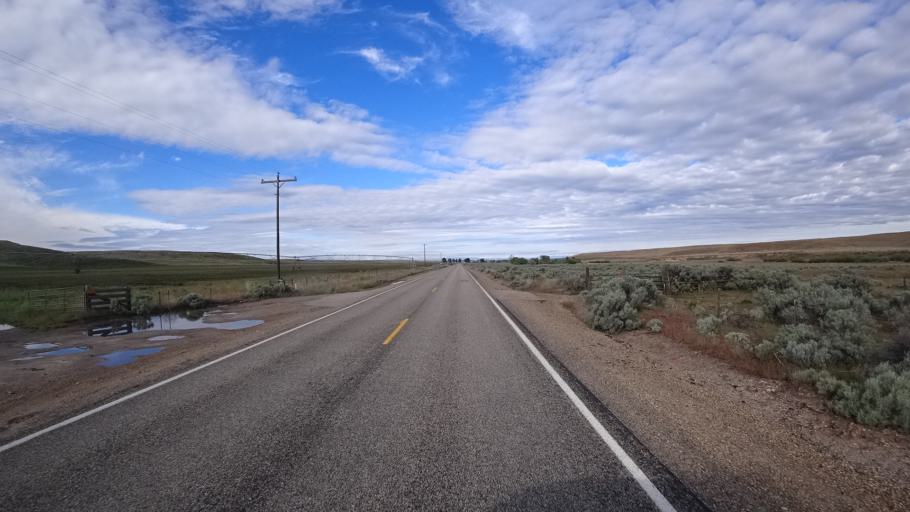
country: US
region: Idaho
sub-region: Ada County
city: Star
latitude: 43.7668
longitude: -116.4984
